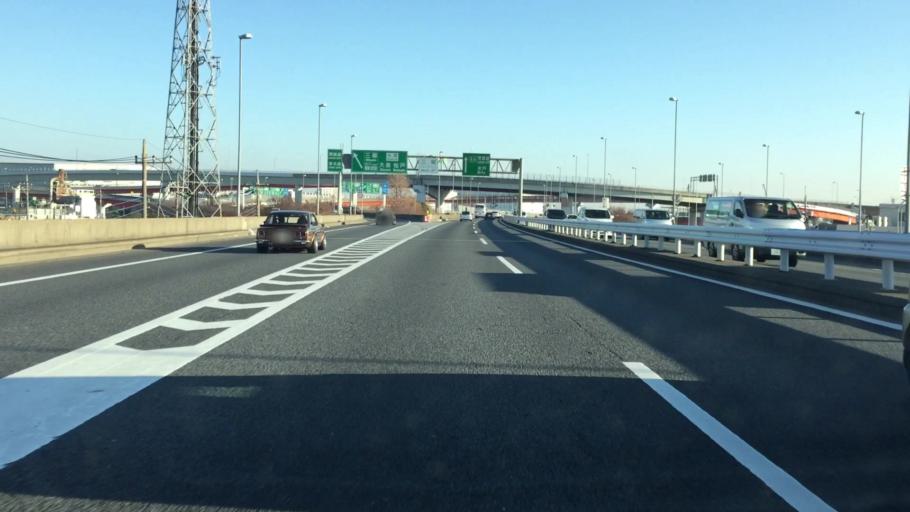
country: JP
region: Saitama
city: Yashio-shi
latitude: 35.8335
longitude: 139.8566
